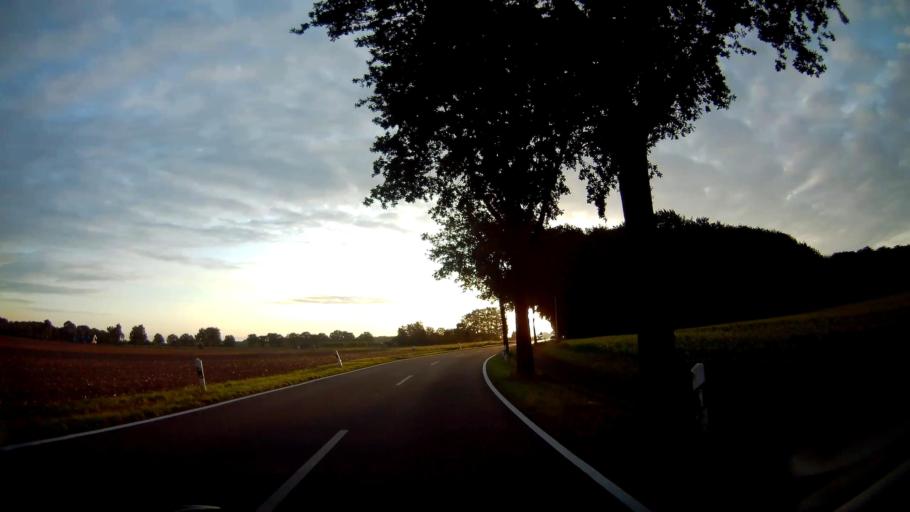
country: DE
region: North Rhine-Westphalia
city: Marl
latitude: 51.6241
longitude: 7.0879
